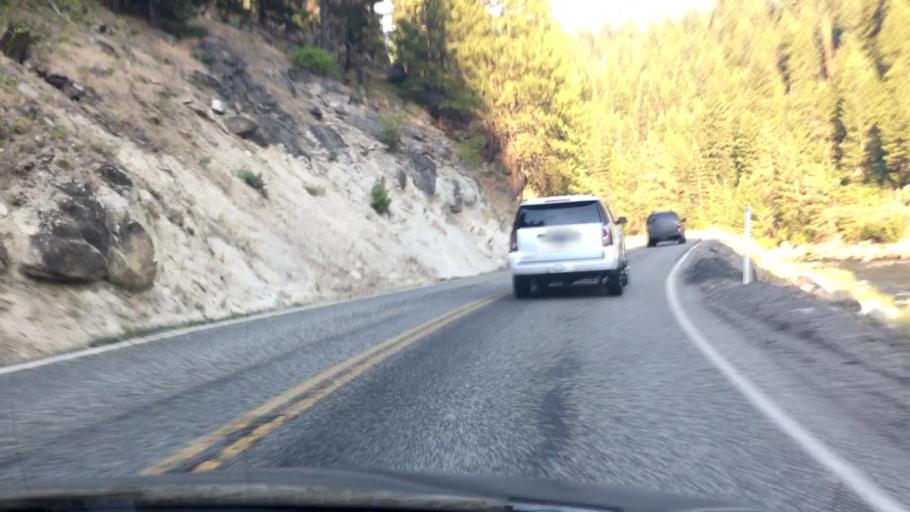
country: US
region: Idaho
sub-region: Valley County
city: Cascade
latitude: 44.3178
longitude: -116.0665
